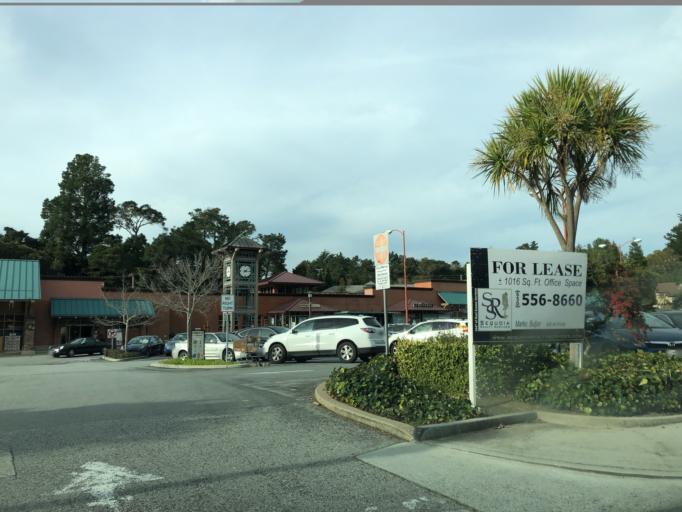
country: US
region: California
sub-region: San Mateo County
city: Highlands-Baywood Park
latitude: 37.5204
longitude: -122.3372
